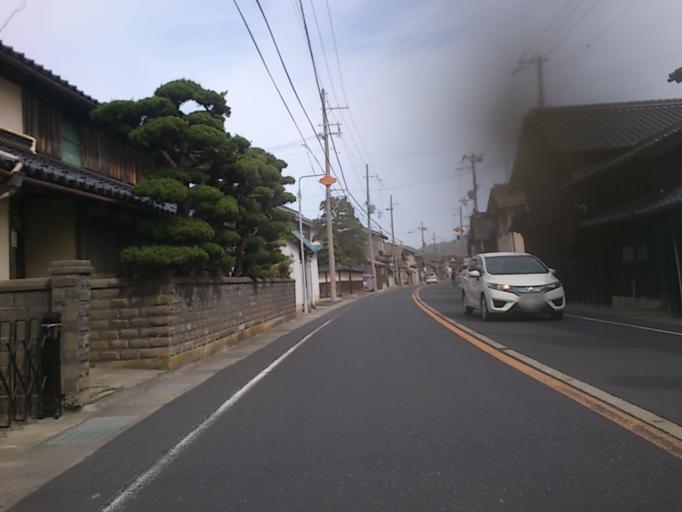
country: JP
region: Kyoto
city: Miyazu
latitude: 35.6886
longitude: 135.0200
